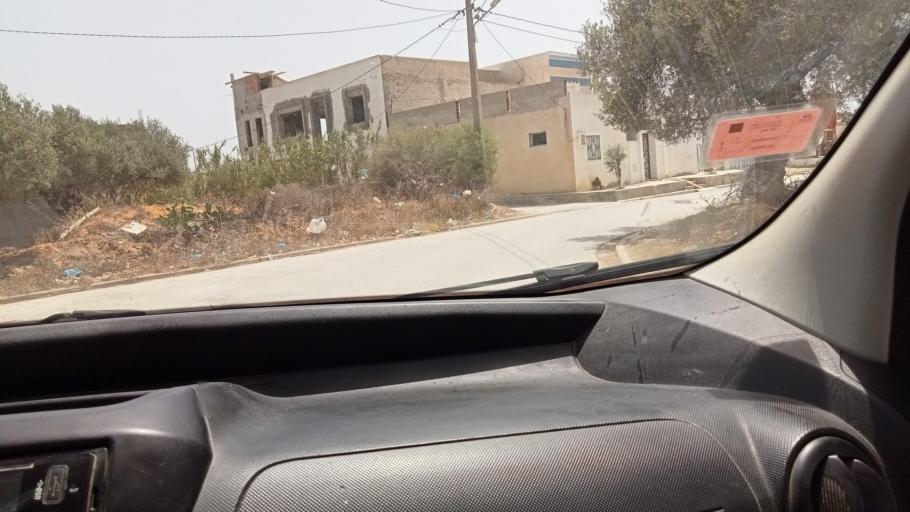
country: TN
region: Nabul
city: Qulaybiyah
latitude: 36.8602
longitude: 11.0843
